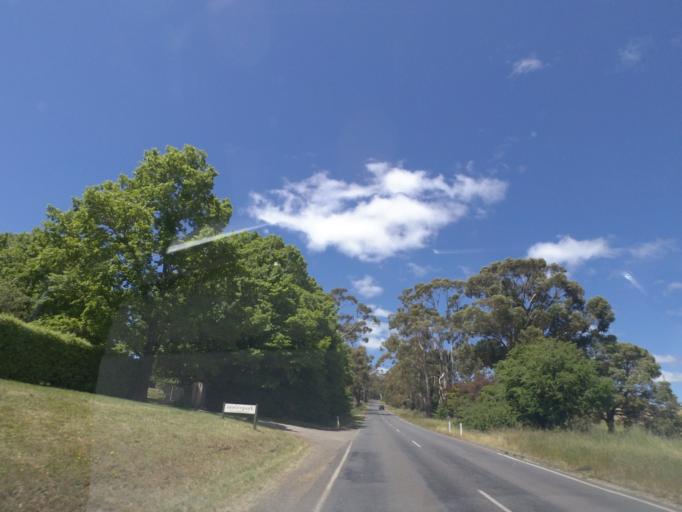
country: AU
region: Victoria
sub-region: Mount Alexander
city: Castlemaine
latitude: -37.2912
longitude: 144.2584
